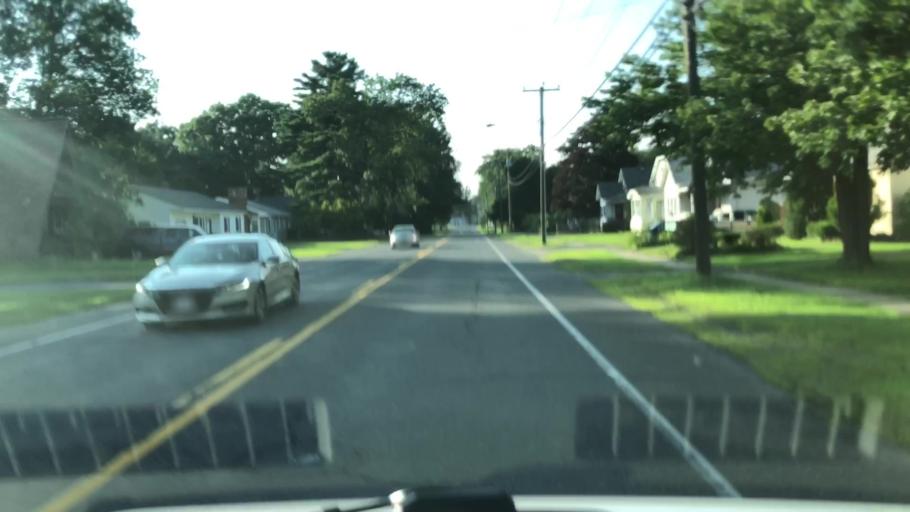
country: US
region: Massachusetts
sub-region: Franklin County
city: Turners Falls
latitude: 42.5962
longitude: -72.5485
